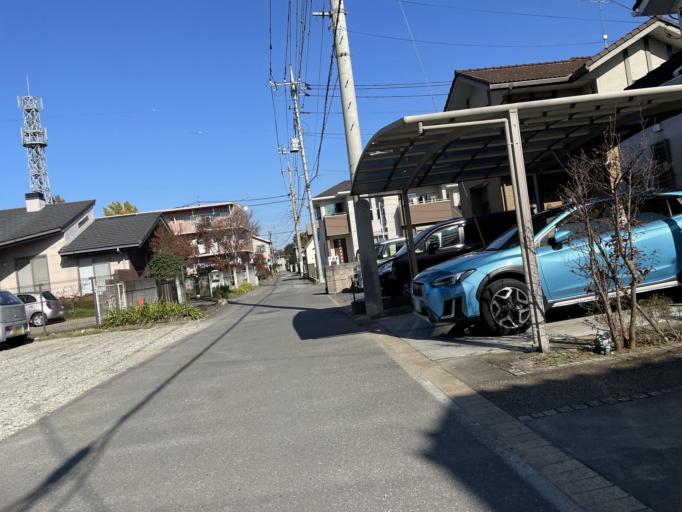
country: JP
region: Gunma
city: Tatebayashi
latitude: 36.2523
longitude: 139.5310
